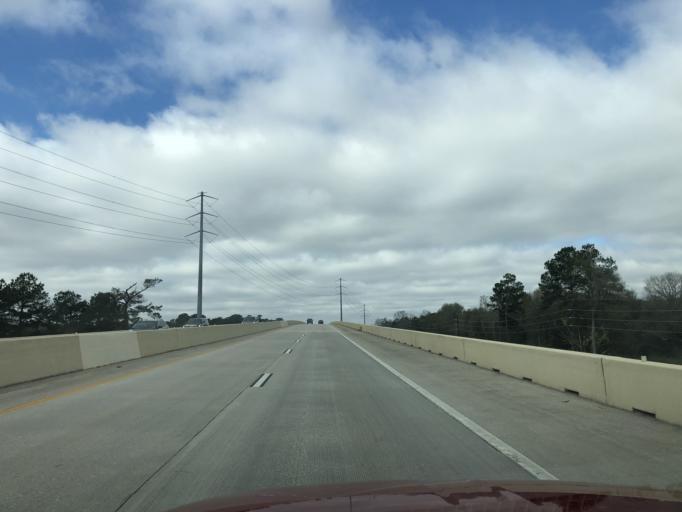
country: US
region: Texas
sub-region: Montgomery County
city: The Woodlands
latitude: 30.0944
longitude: -95.4896
